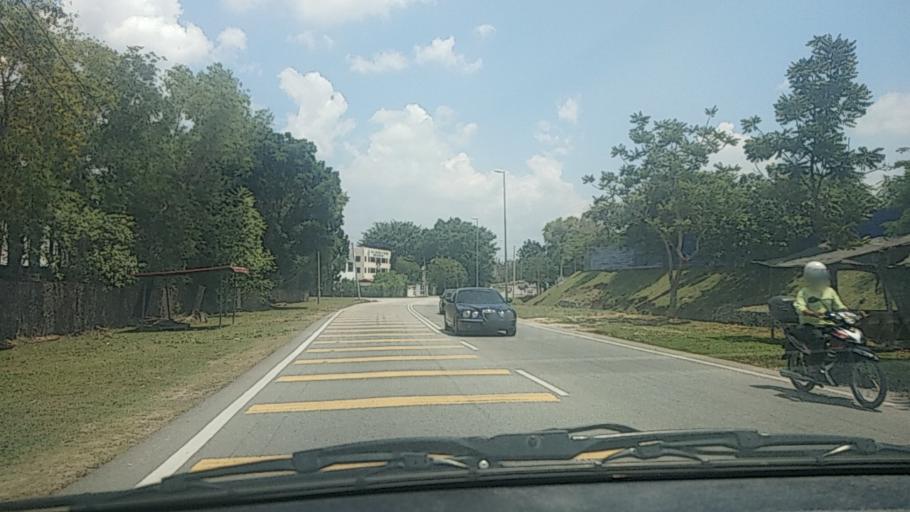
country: MY
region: Kedah
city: Sungai Petani
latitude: 5.6460
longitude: 100.5343
